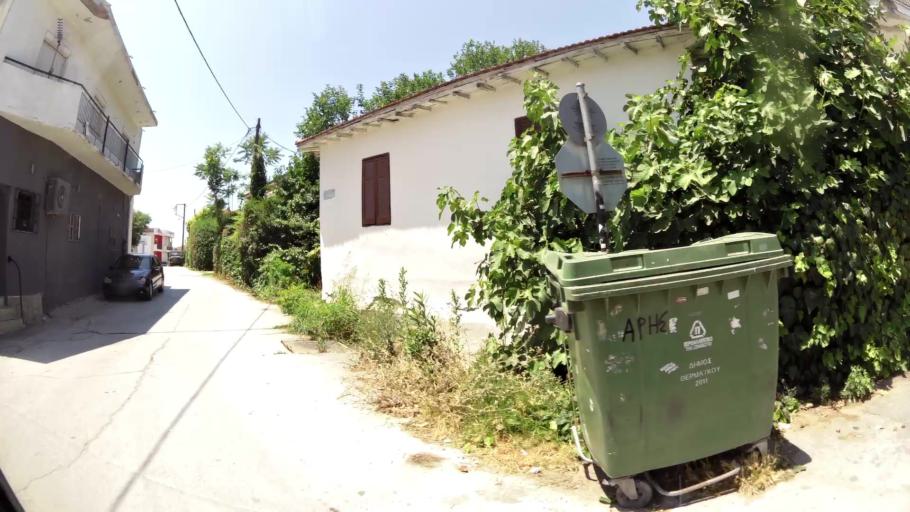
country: GR
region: Central Macedonia
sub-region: Nomos Thessalonikis
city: Epanomi
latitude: 40.4281
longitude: 22.9266
